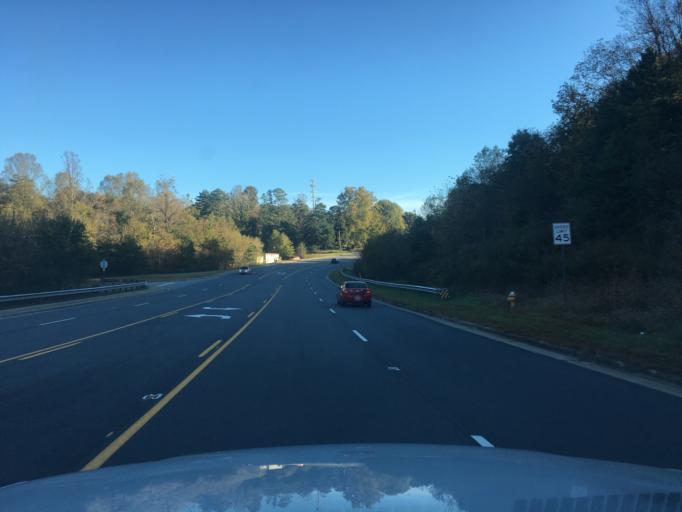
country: US
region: North Carolina
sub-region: Catawba County
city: Mountain View
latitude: 35.7041
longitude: -81.3485
